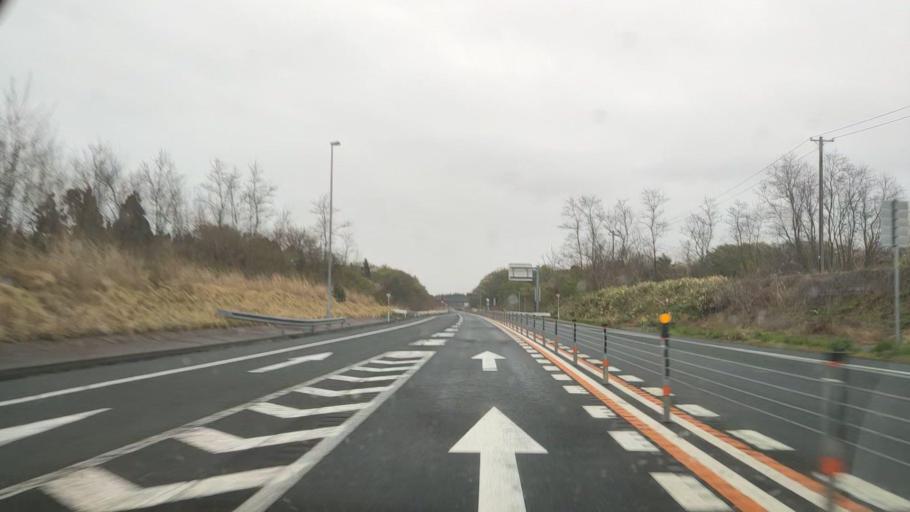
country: JP
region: Akita
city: Noshiromachi
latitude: 40.1509
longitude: 140.0214
